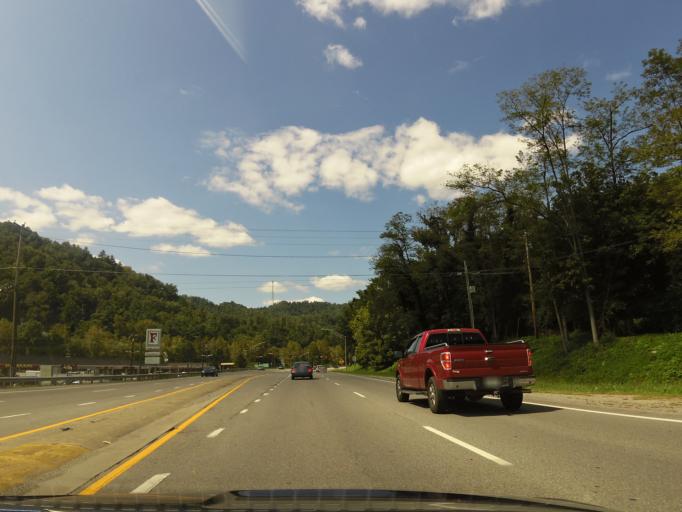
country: US
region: Kentucky
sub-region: Harlan County
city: Harlan
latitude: 36.8254
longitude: -83.3207
